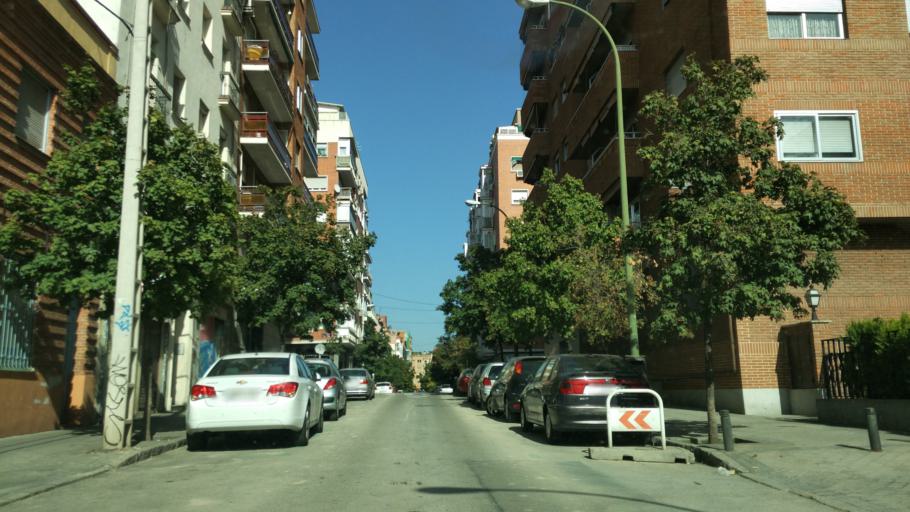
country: ES
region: Madrid
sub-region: Provincia de Madrid
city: Tetuan de las Victorias
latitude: 40.4566
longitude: -3.6999
